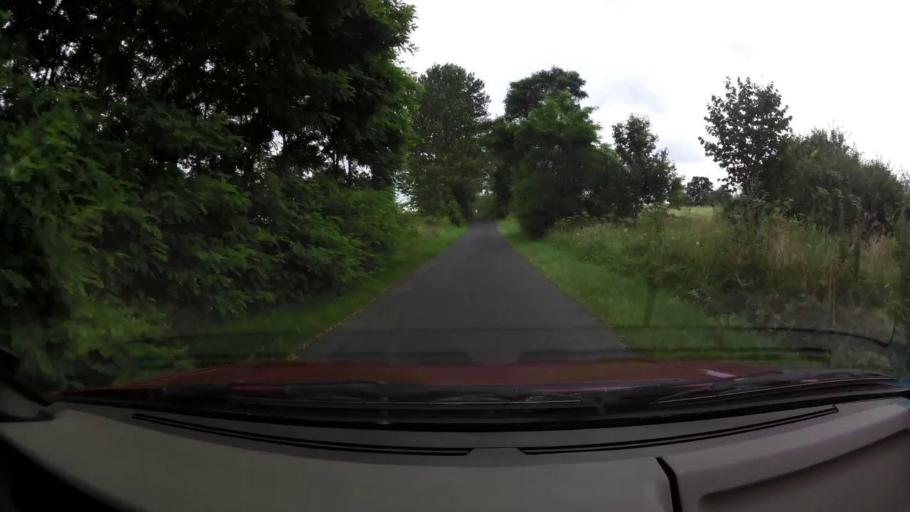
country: PL
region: West Pomeranian Voivodeship
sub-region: Powiat drawski
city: Drawsko Pomorskie
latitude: 53.5232
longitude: 15.7565
